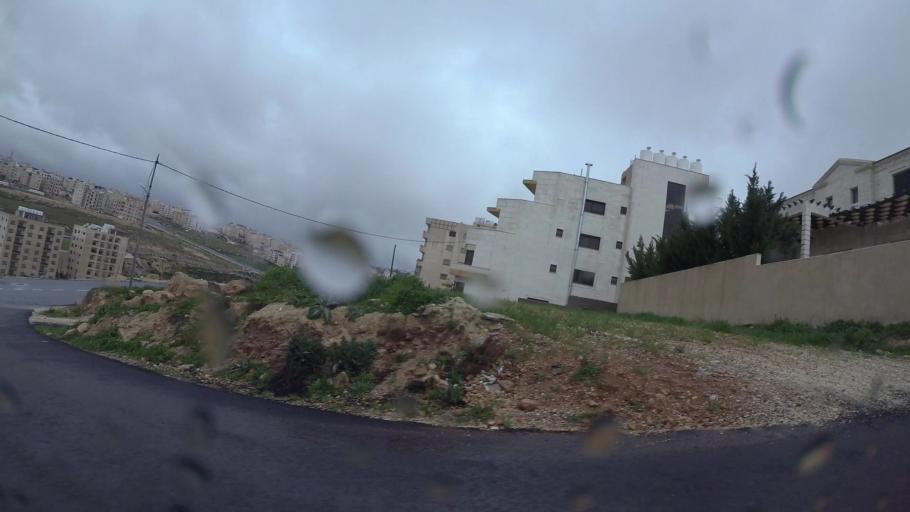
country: JO
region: Amman
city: Al Jubayhah
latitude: 32.0417
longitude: 35.8885
